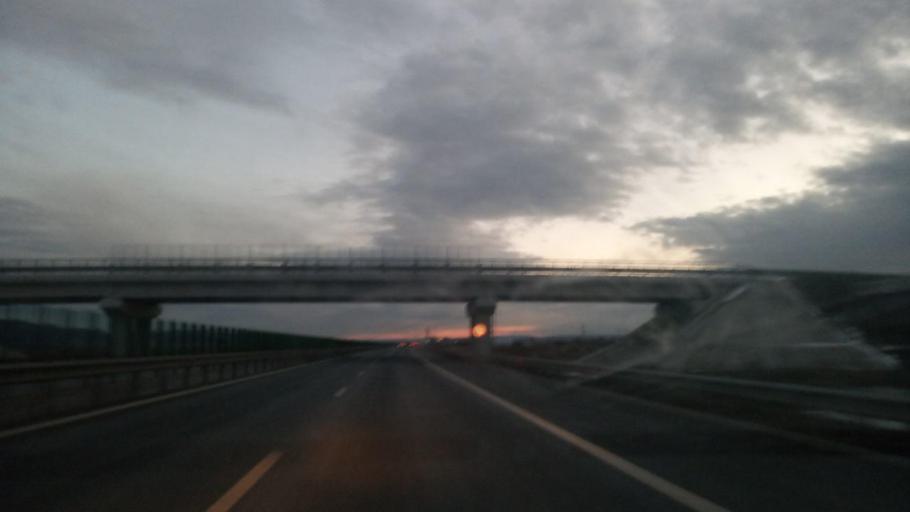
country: RO
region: Bacau
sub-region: Comuna Letea Veche
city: Letea Veche
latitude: 46.5573
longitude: 26.9679
